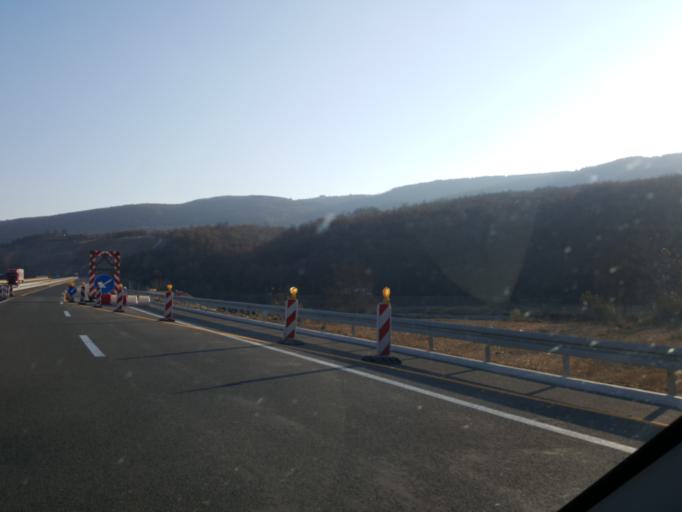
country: RS
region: Central Serbia
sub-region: Pirotski Okrug
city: Dimitrovgrad
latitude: 43.0126
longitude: 22.8028
